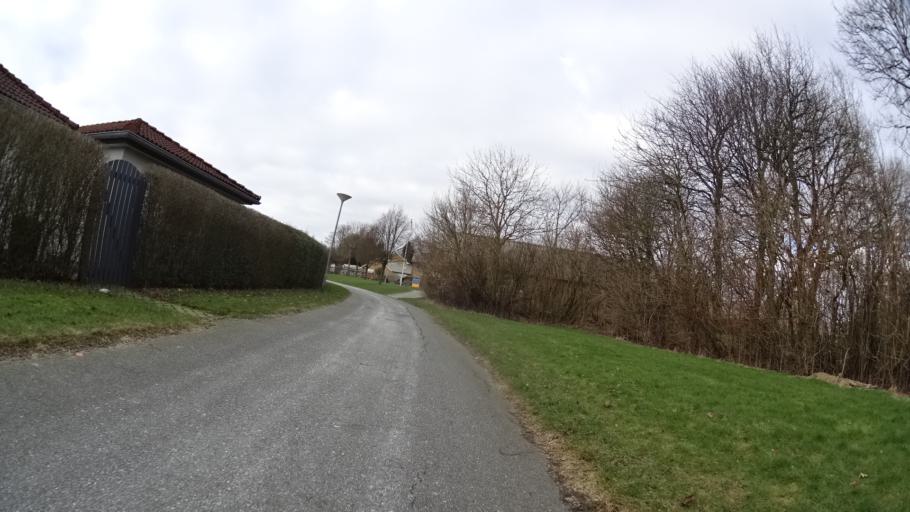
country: DK
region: Central Jutland
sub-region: Arhus Kommune
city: Tranbjerg
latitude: 56.0976
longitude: 10.1231
